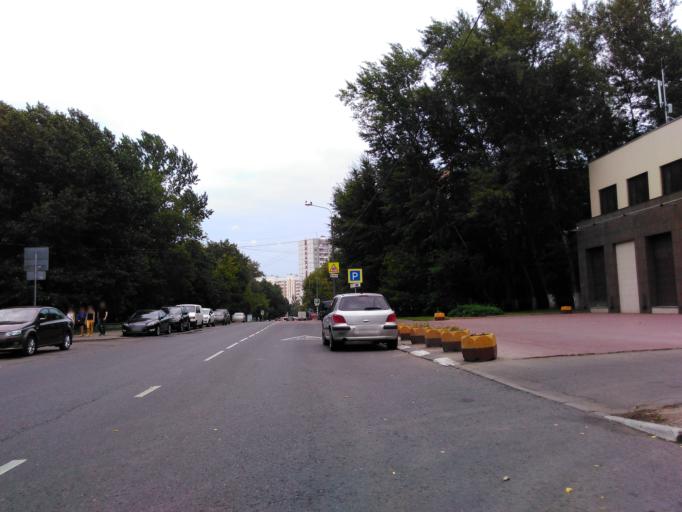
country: RU
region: Moscow
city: Novyye Cheremushki
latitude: 55.6851
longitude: 37.5960
